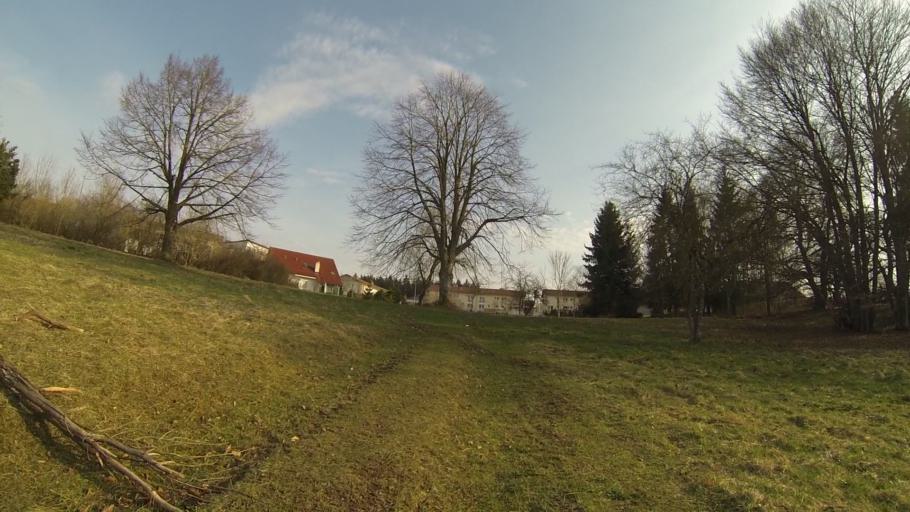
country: DE
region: Baden-Wuerttemberg
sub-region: Regierungsbezirk Stuttgart
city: Heidenheim an der Brenz
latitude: 48.6588
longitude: 10.1355
